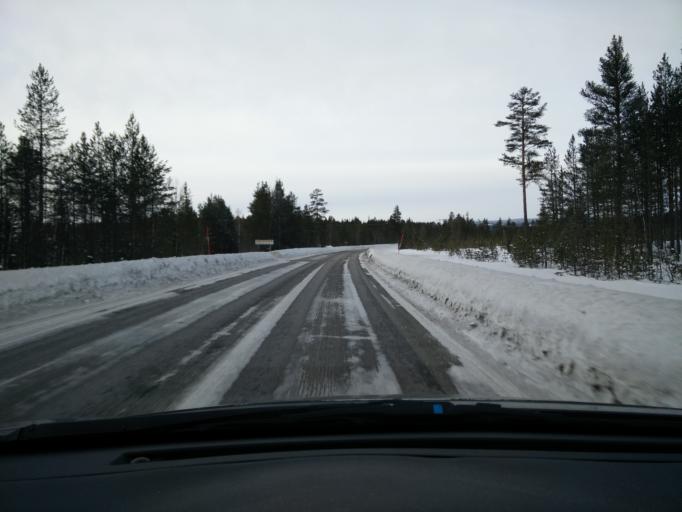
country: SE
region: Jaemtland
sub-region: Harjedalens Kommun
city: Sveg
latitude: 62.4359
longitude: 13.8799
